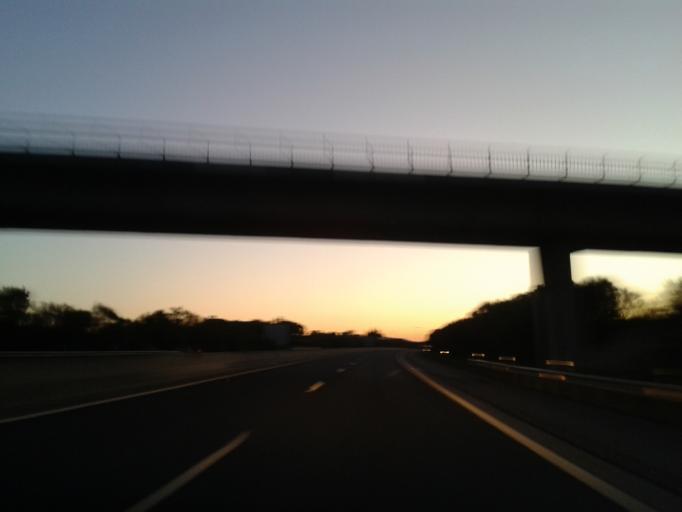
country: PT
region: Faro
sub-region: Albufeira
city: Guia
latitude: 37.1393
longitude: -8.3336
